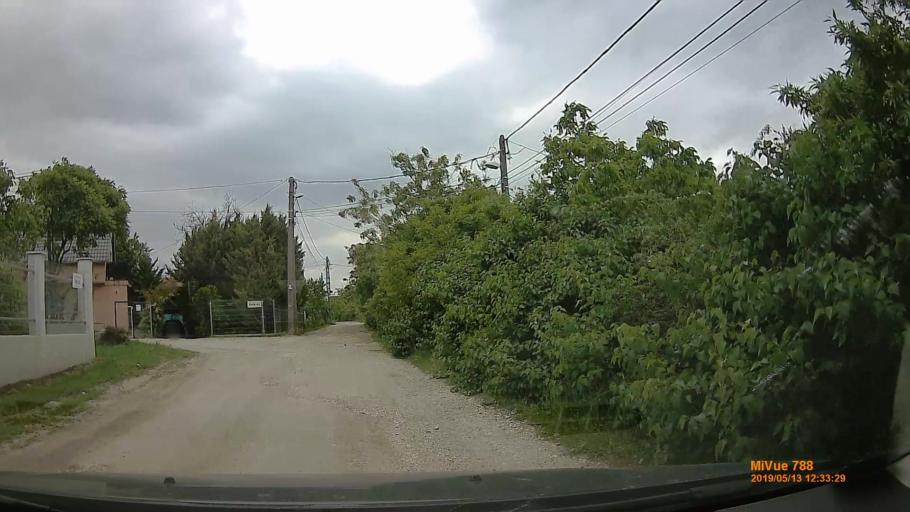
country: HU
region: Pest
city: Diosd
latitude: 47.4076
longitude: 18.9861
